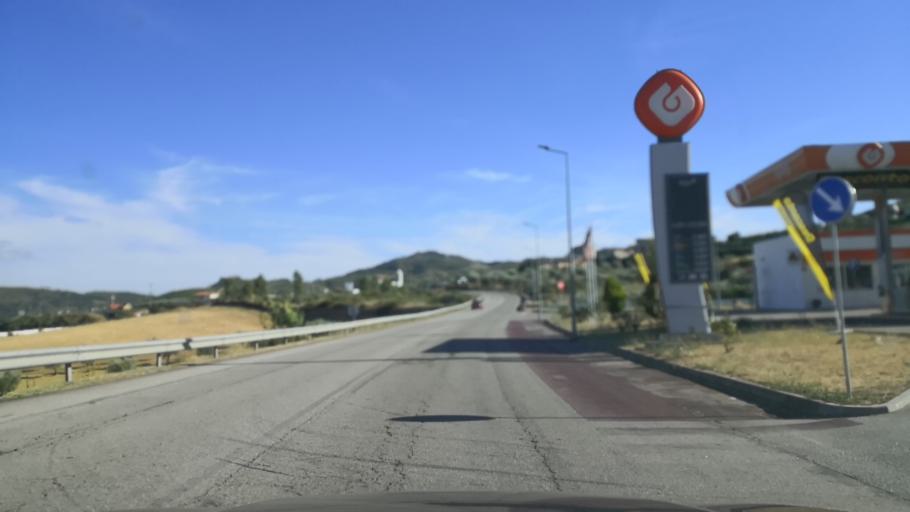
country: PT
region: Vila Real
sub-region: Murca
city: Murca
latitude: 41.4018
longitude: -7.4466
